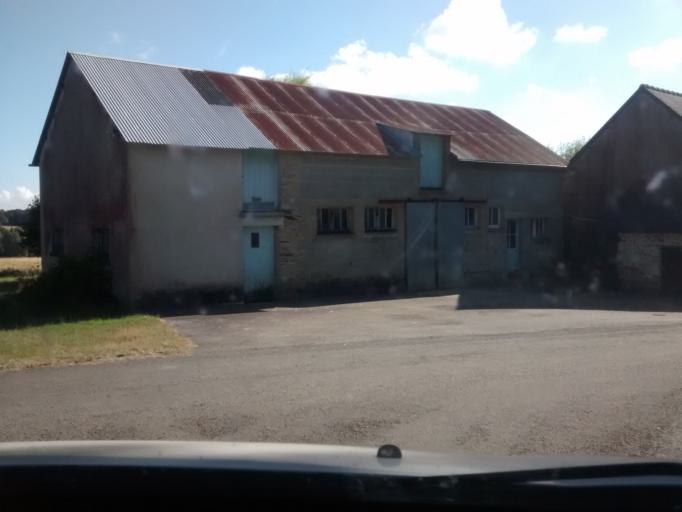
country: FR
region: Brittany
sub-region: Departement d'Ille-et-Vilaine
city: Bain-de-Bretagne
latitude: 47.8553
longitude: -1.7248
